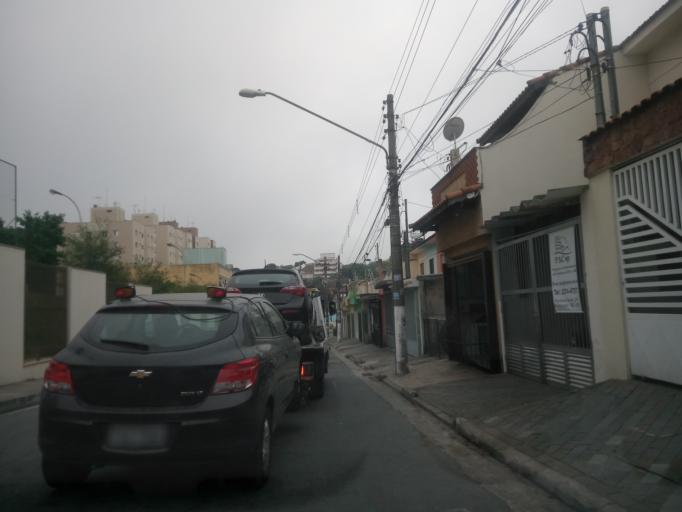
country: BR
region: Sao Paulo
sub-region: Sao Bernardo Do Campo
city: Sao Bernardo do Campo
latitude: -23.7231
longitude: -46.5674
